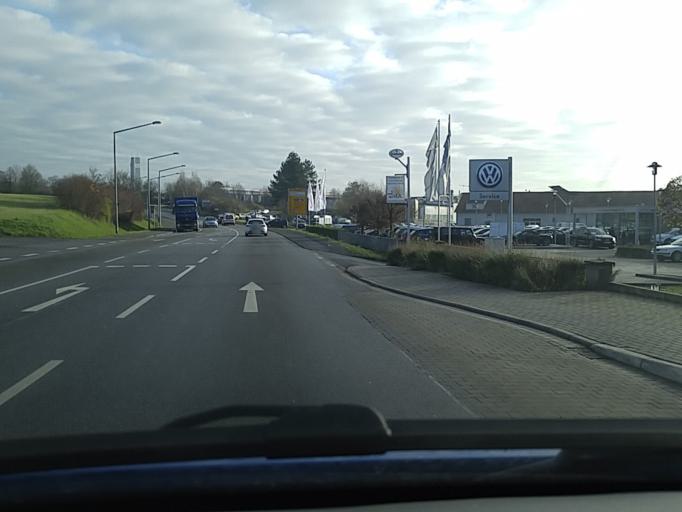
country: DE
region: Hesse
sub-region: Regierungsbezirk Darmstadt
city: Bad Nauheim
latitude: 50.3577
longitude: 8.7464
